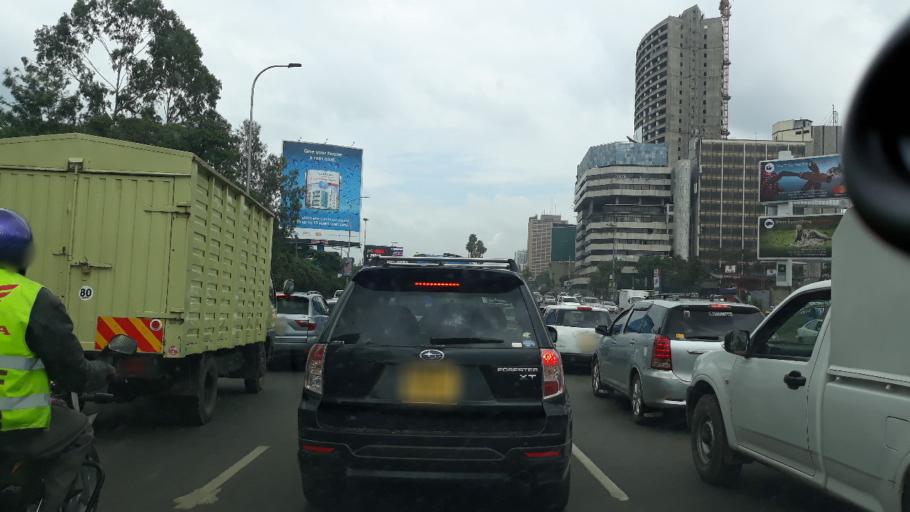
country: KE
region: Nairobi Area
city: Nairobi
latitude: -1.2941
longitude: 36.8211
